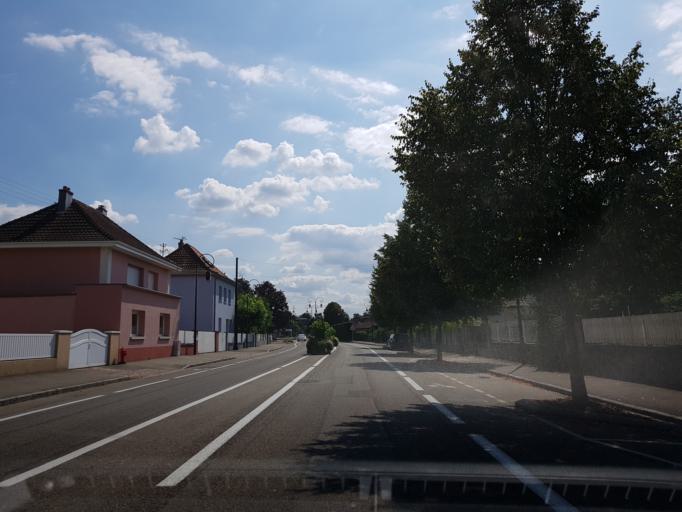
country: FR
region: Alsace
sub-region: Departement du Haut-Rhin
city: Sausheim
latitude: 47.7864
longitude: 7.3680
